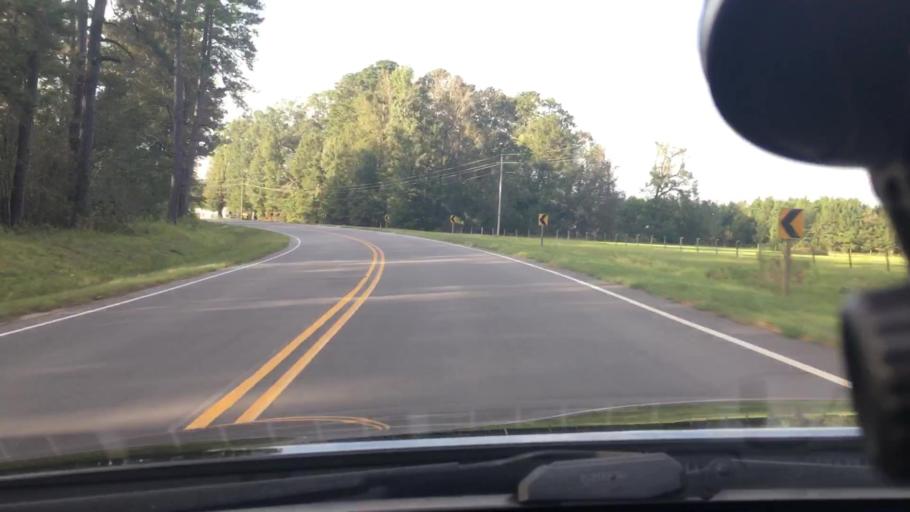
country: US
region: North Carolina
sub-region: Pitt County
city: Windsor
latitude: 35.4518
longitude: -77.2638
